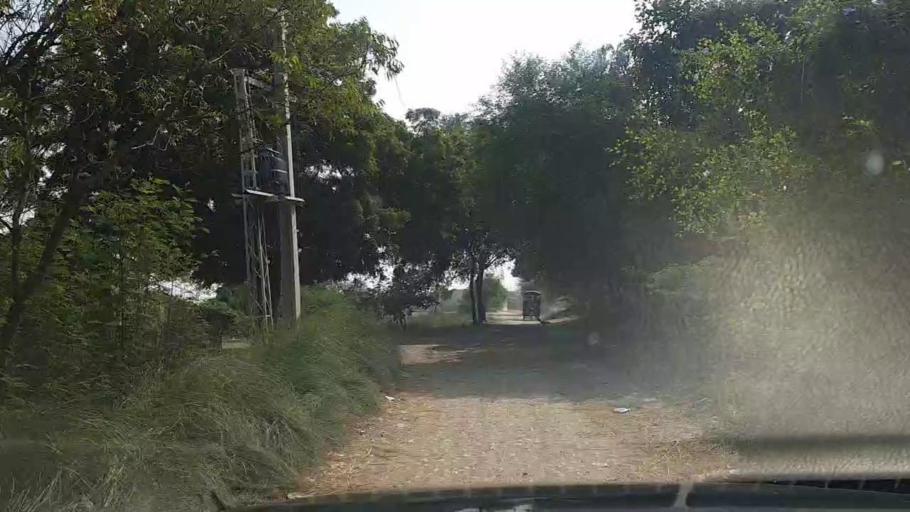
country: PK
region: Sindh
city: Mirpur Batoro
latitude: 24.7053
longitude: 68.2162
